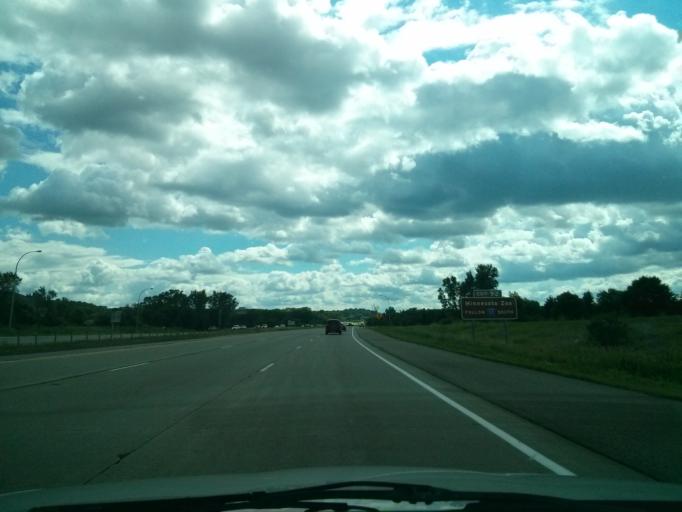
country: US
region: Minnesota
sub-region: Dakota County
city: Eagan
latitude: 44.7890
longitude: -93.2030
